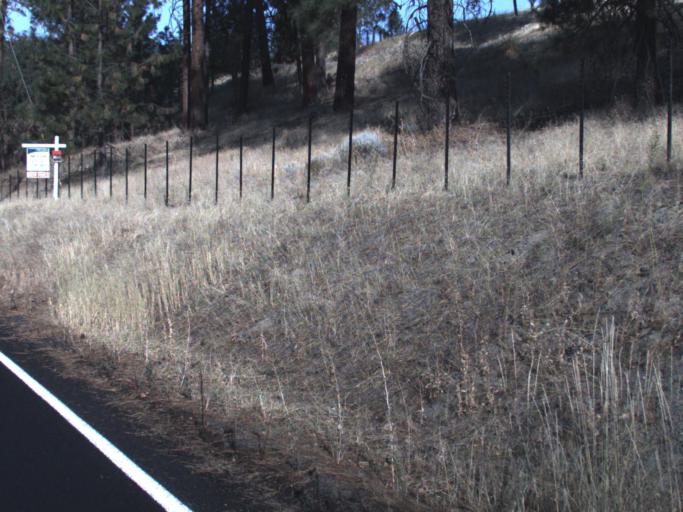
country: US
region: Washington
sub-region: Spokane County
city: Deer Park
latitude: 47.8920
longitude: -117.6779
